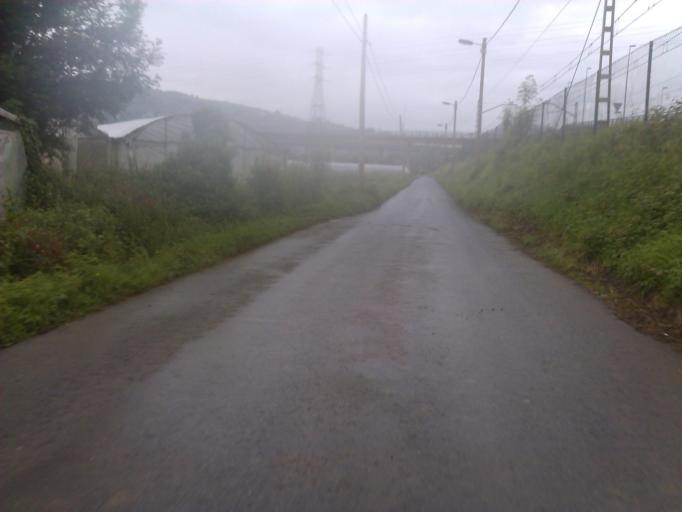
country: ES
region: Basque Country
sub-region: Provincia de Guipuzcoa
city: Astigarraga
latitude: 43.2905
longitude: -1.9558
